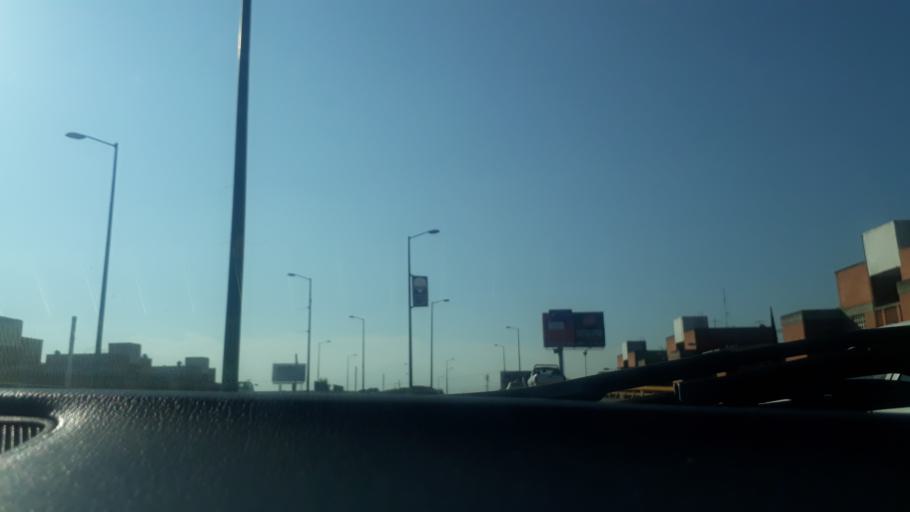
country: MX
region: Puebla
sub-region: Puebla
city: El Capulo (La Quebradora)
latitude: 18.9915
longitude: -98.2438
